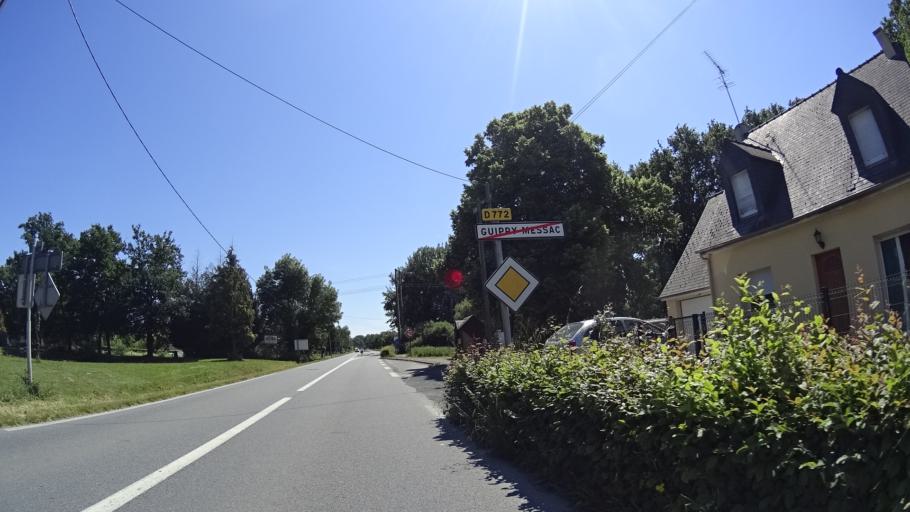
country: FR
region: Brittany
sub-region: Departement d'Ille-et-Vilaine
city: Messac
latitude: 47.8255
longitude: -1.7918
